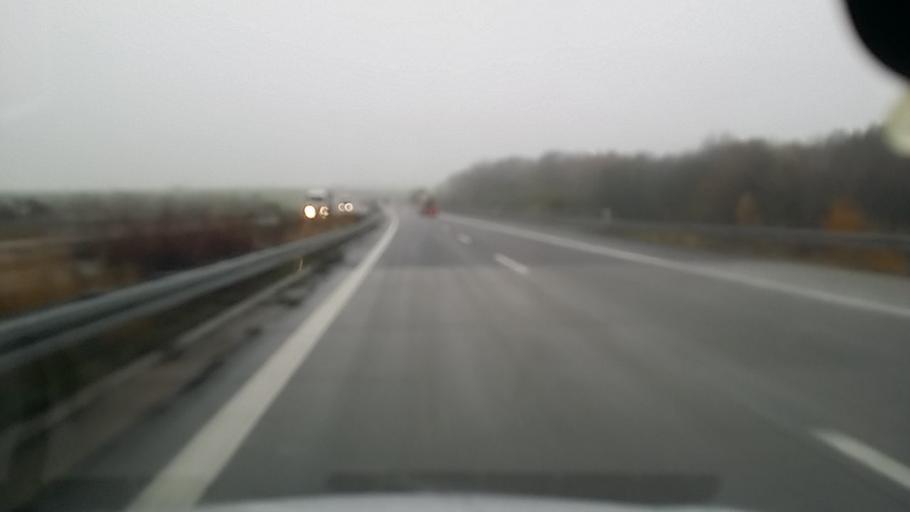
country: DE
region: Saxony
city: Liebstadt
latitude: 50.8698
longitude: 13.8711
